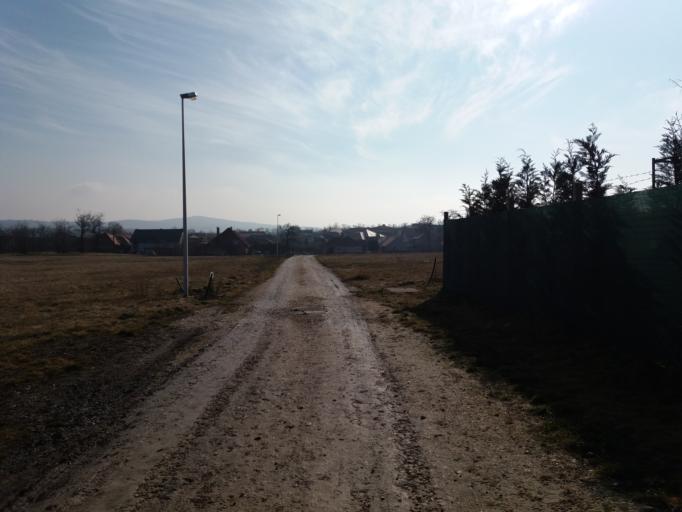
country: HU
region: Pest
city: Paty
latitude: 47.5193
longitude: 18.8080
